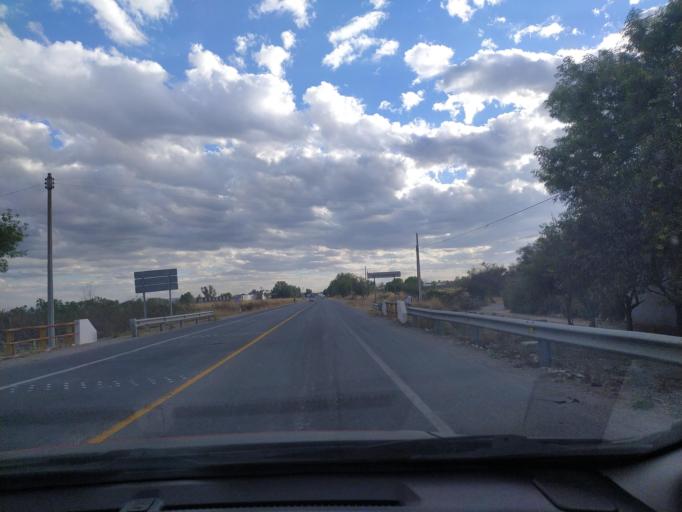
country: LA
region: Oudomxai
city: Muang La
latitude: 21.0204
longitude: 101.8266
